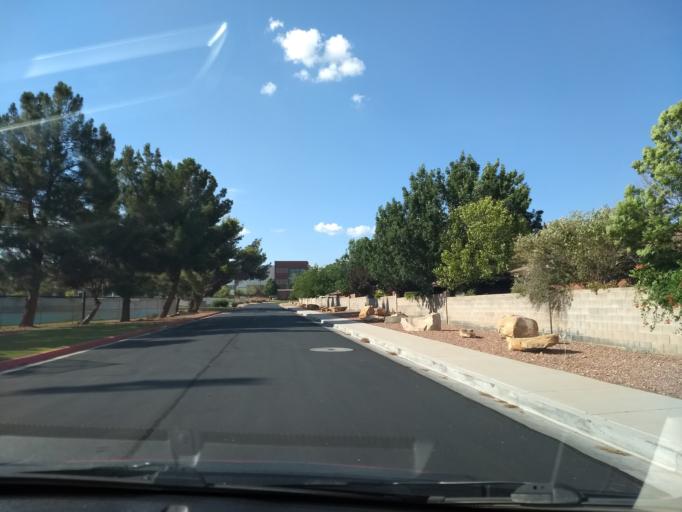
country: US
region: Utah
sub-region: Washington County
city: Saint George
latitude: 37.0928
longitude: -113.5775
